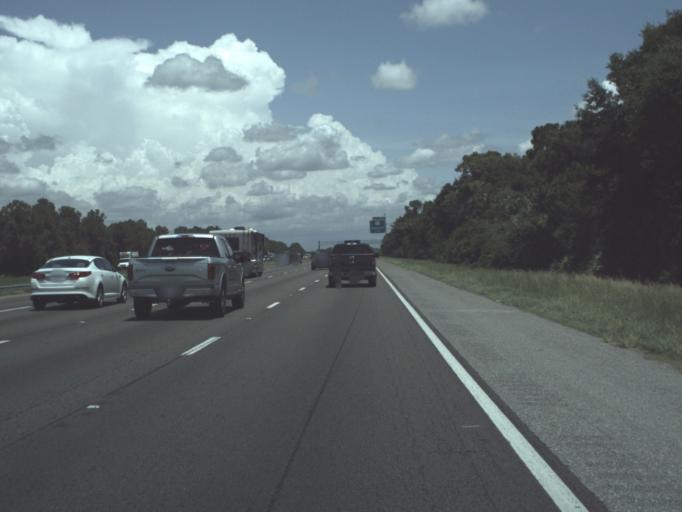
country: US
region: Florida
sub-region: Hillsborough County
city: Riverview
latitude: 27.8793
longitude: -82.3479
